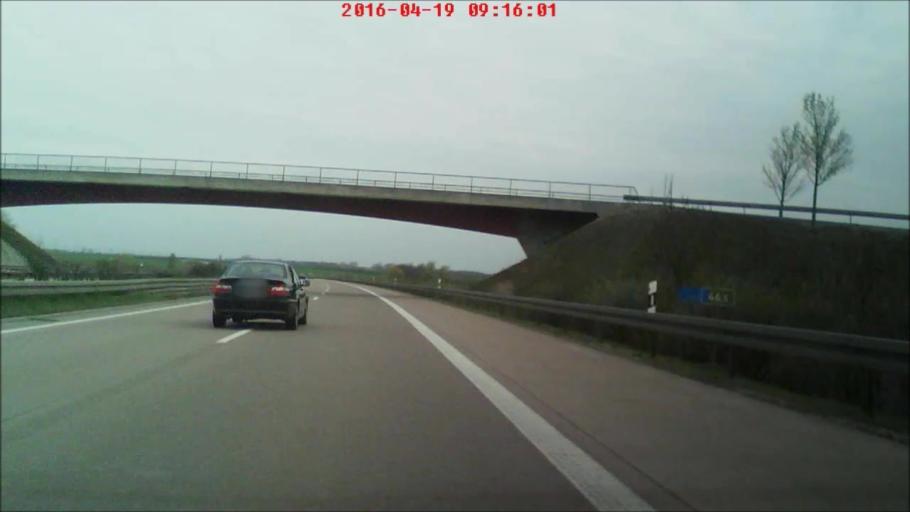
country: DE
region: Thuringia
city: Eckstedt
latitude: 51.0744
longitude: 11.1234
